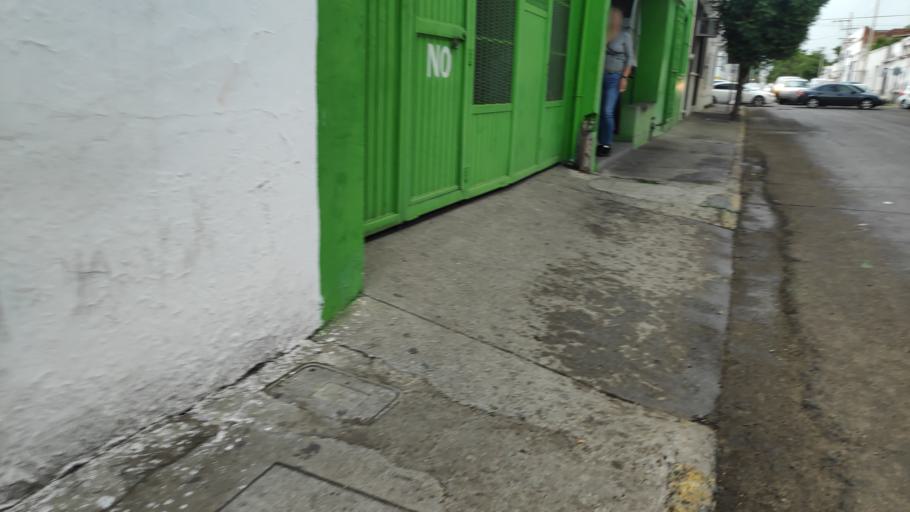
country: MX
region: Sinaloa
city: Culiacan
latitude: 24.8069
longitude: -107.4018
